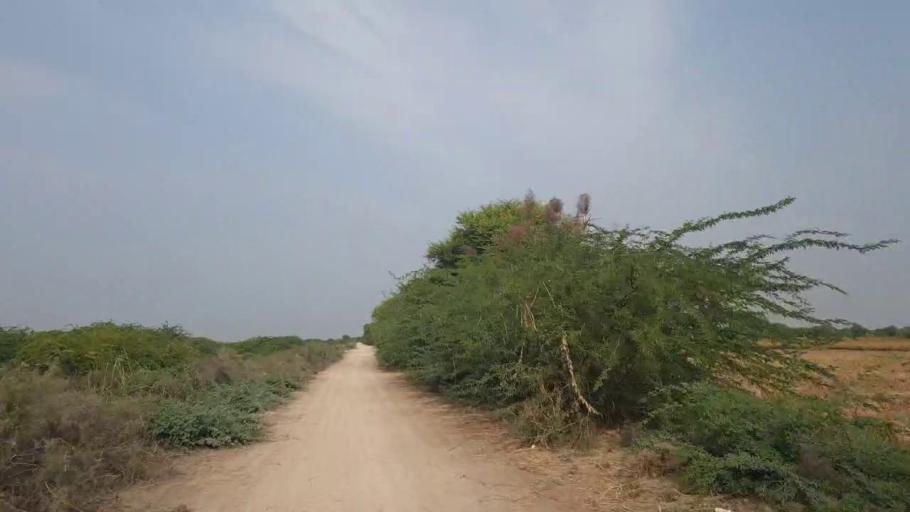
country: PK
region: Sindh
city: Badin
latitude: 24.5602
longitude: 68.7328
